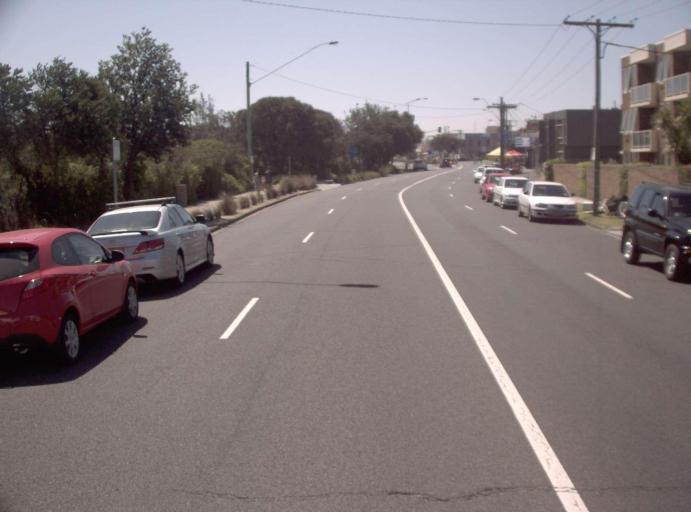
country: AU
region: Victoria
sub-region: Bayside
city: Black Rock
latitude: -37.9773
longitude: 145.0167
